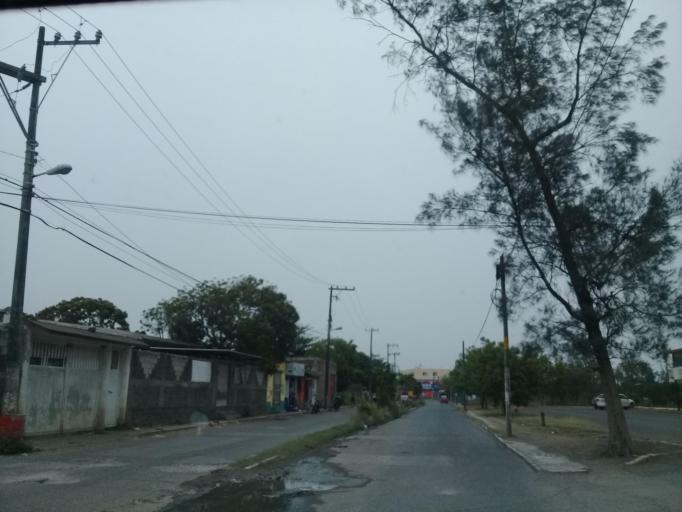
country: MX
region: Veracruz
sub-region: Veracruz
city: Las Amapolas
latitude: 19.1592
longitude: -96.2080
